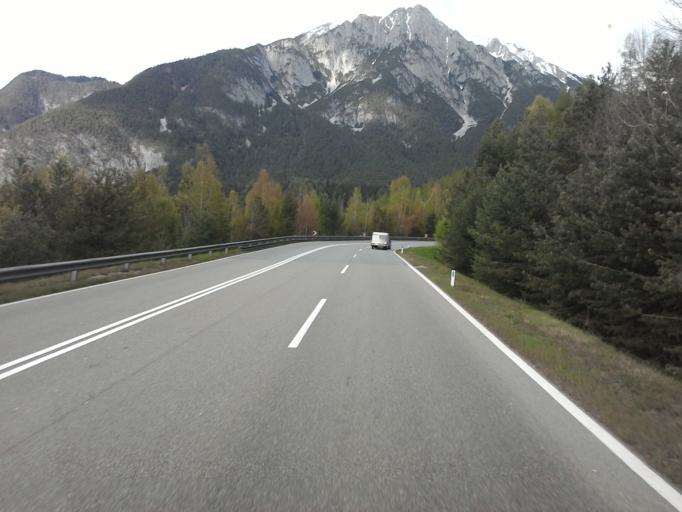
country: AT
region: Tyrol
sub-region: Politischer Bezirk Imst
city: Nassereith
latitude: 47.3049
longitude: 10.8556
